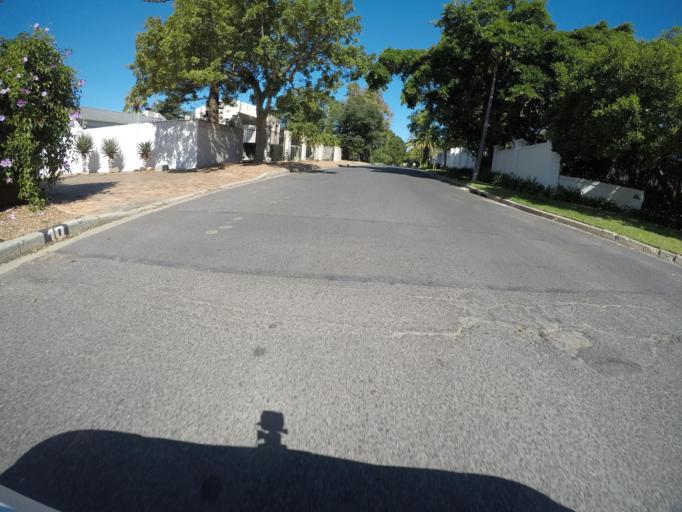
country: ZA
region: Western Cape
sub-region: City of Cape Town
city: Kraaifontein
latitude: -33.8627
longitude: 18.6482
